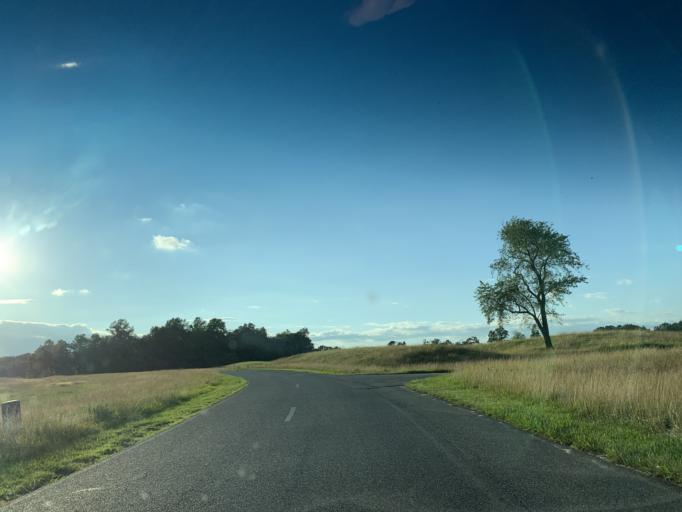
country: US
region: Maryland
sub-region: Harford County
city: Havre de Grace
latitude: 39.5379
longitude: -76.1302
